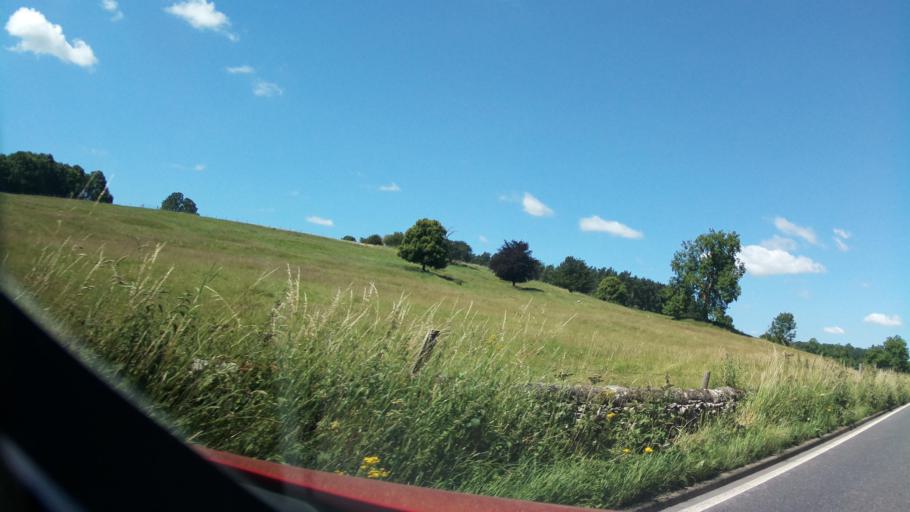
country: GB
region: England
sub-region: Derbyshire
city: Bakewell
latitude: 53.1940
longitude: -1.6552
